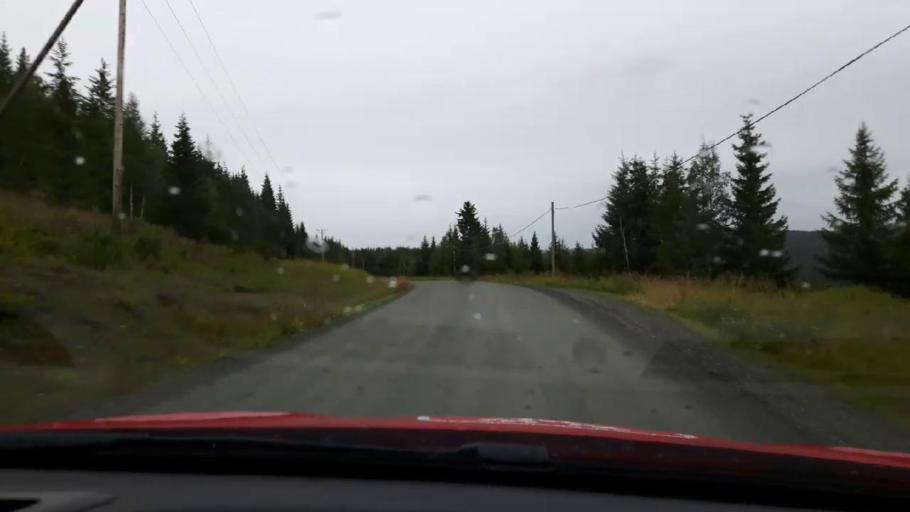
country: SE
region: Jaemtland
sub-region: Are Kommun
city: Are
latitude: 63.4122
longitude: 12.8283
